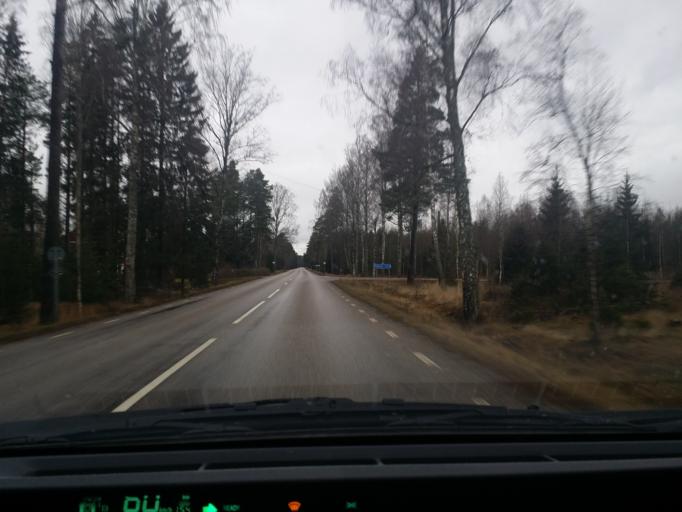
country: SE
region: Vaestmanland
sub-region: Sala Kommun
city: Sala
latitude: 59.8258
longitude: 16.5228
